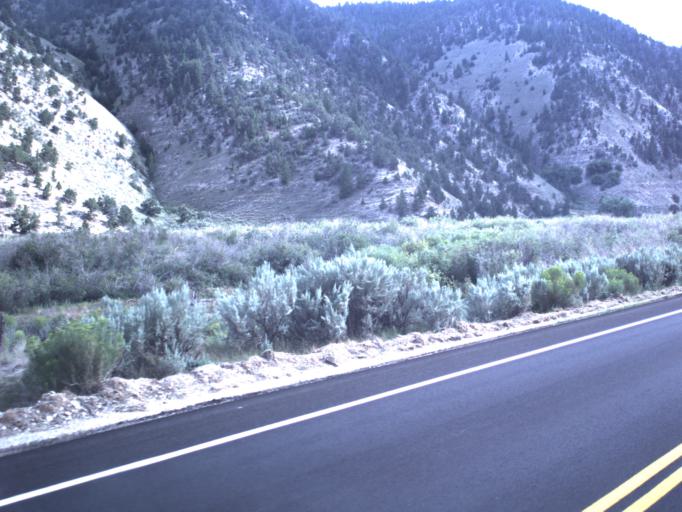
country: US
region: Utah
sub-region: Duchesne County
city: Duchesne
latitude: 40.0125
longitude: -110.5656
